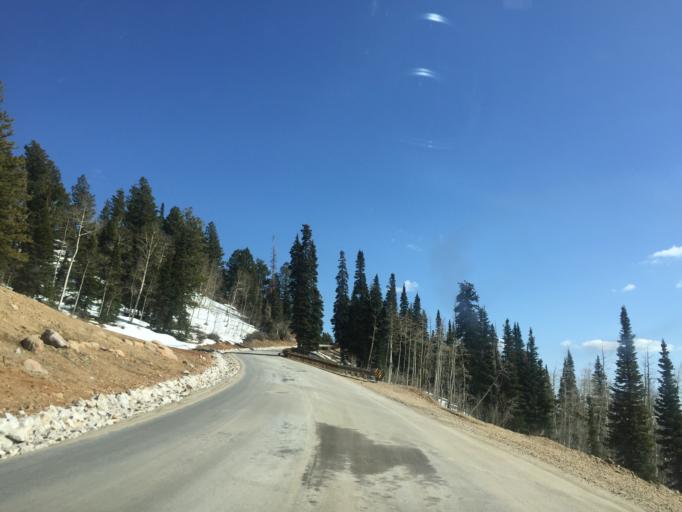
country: US
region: Utah
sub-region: Weber County
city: Wolf Creek
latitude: 41.3776
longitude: -111.7812
